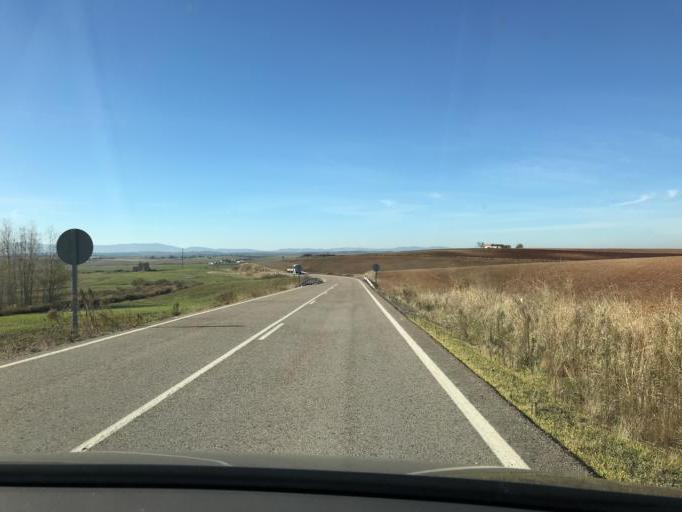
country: ES
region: Extremadura
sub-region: Provincia de Badajoz
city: Azuaga
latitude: 38.2585
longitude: -5.7228
